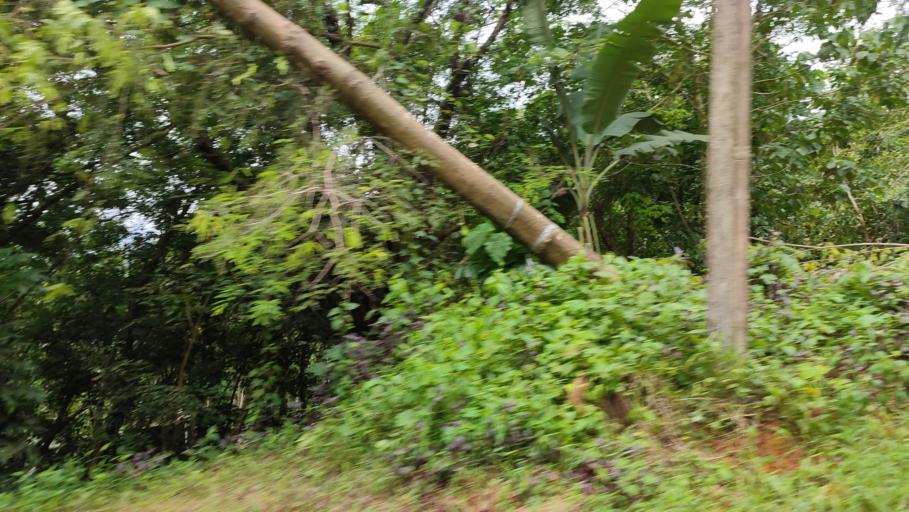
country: IN
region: Kerala
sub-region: Kasaragod District
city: Nileshwar
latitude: 12.2928
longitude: 75.2729
